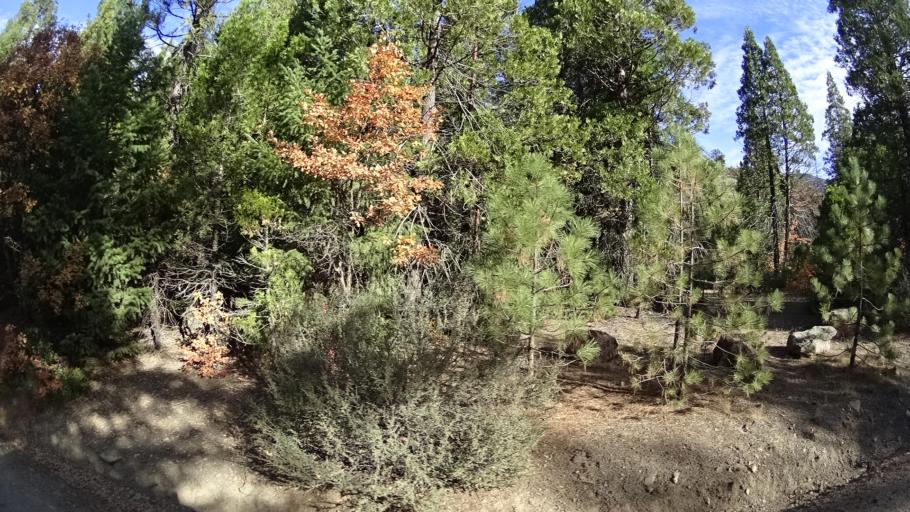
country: US
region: California
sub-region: Siskiyou County
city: Yreka
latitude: 41.7170
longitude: -122.7785
